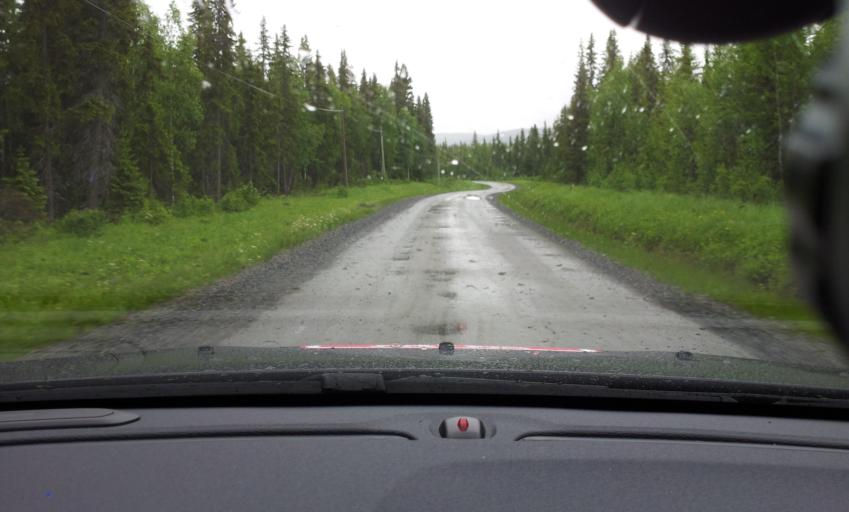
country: SE
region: Jaemtland
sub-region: Are Kommun
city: Are
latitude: 63.4411
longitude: 12.8078
